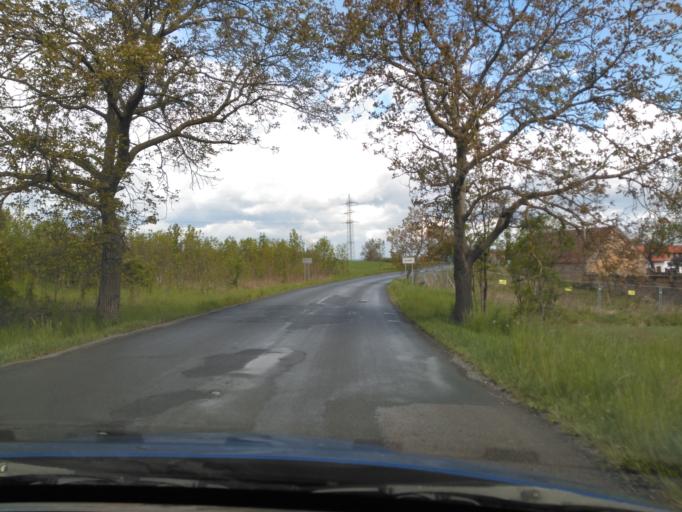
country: CZ
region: Central Bohemia
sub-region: Okres Beroun
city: Beroun
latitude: 49.9367
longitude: 14.0723
